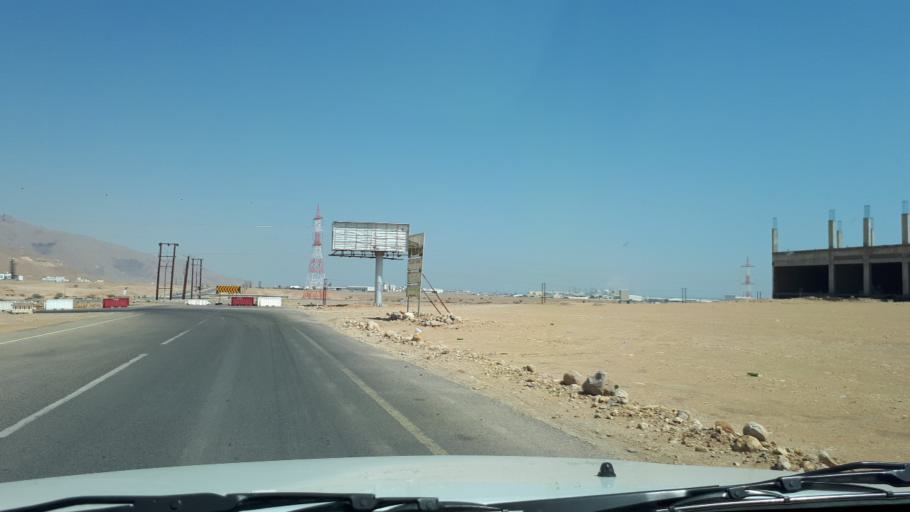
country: OM
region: Ash Sharqiyah
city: Sur
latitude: 22.6026
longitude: 59.4321
